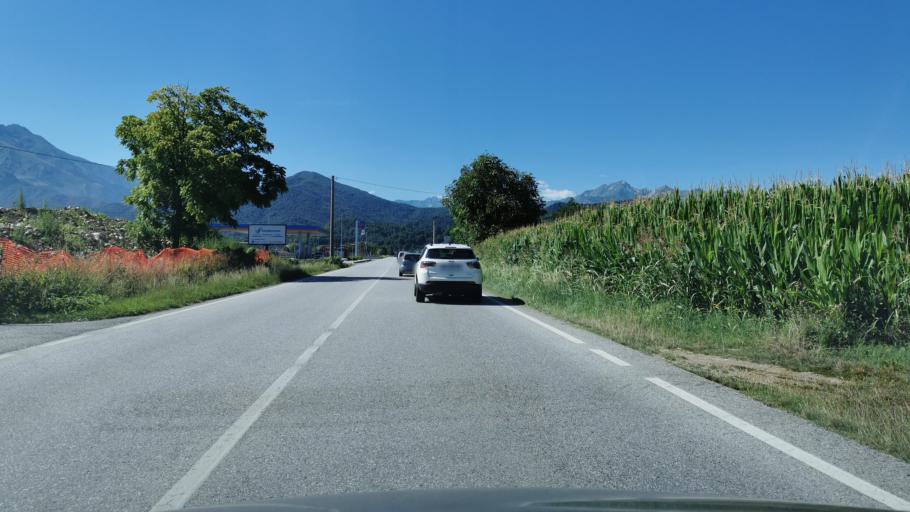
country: IT
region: Piedmont
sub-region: Provincia di Cuneo
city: Boves
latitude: 44.3484
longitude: 7.5461
